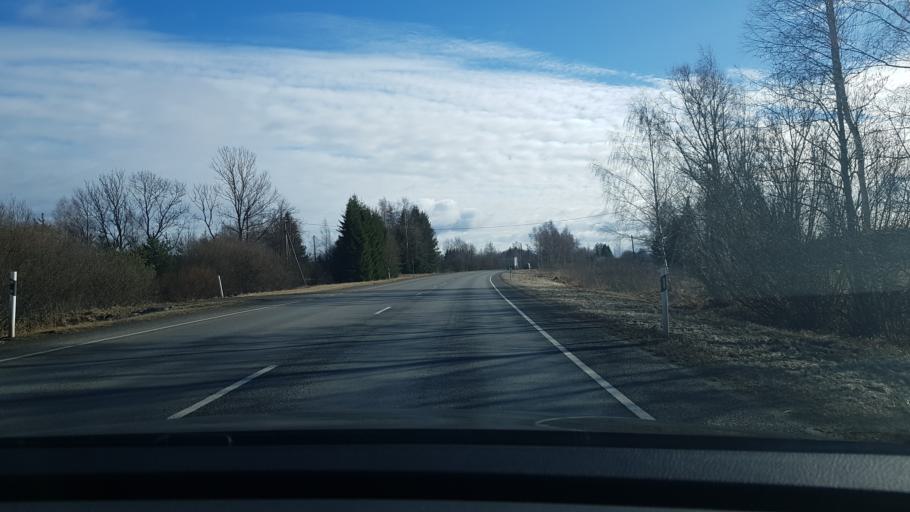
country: EE
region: Paernumaa
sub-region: Saarde vald
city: Kilingi-Nomme
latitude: 58.1883
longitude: 24.7838
